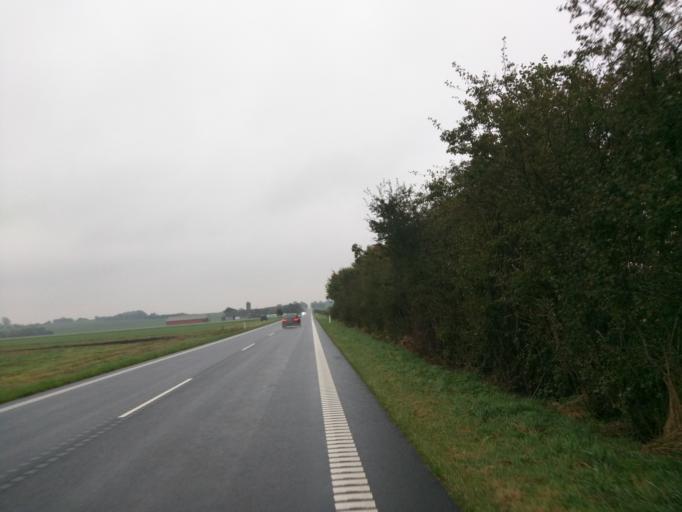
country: DK
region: Central Jutland
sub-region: Silkeborg Kommune
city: Kjellerup
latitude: 56.3668
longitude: 9.4386
